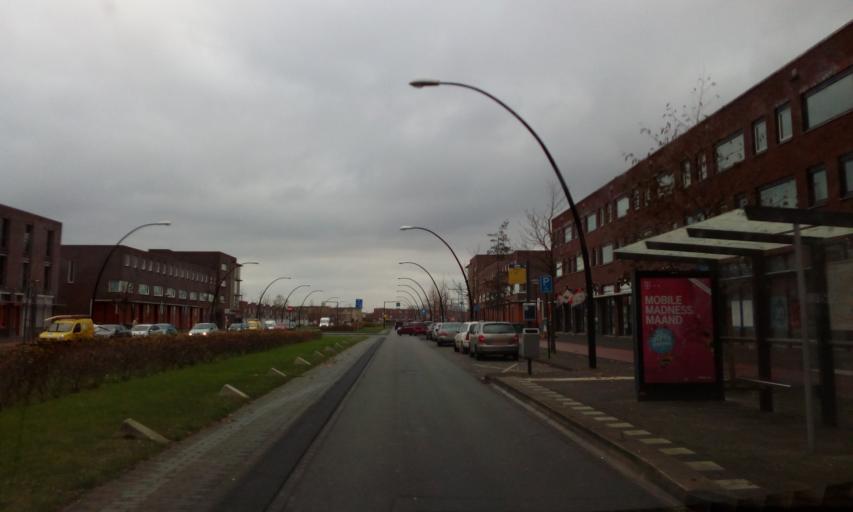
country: NL
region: South Holland
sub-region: Gemeente Rijswijk
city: Rijswijk
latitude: 52.0199
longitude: 4.2977
